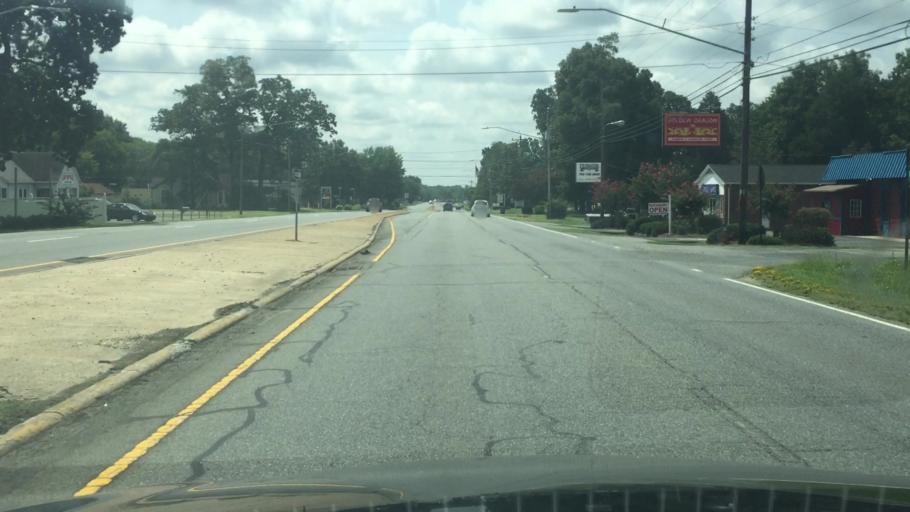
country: US
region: North Carolina
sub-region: Cabarrus County
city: Kannapolis
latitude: 35.4634
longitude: -80.6094
